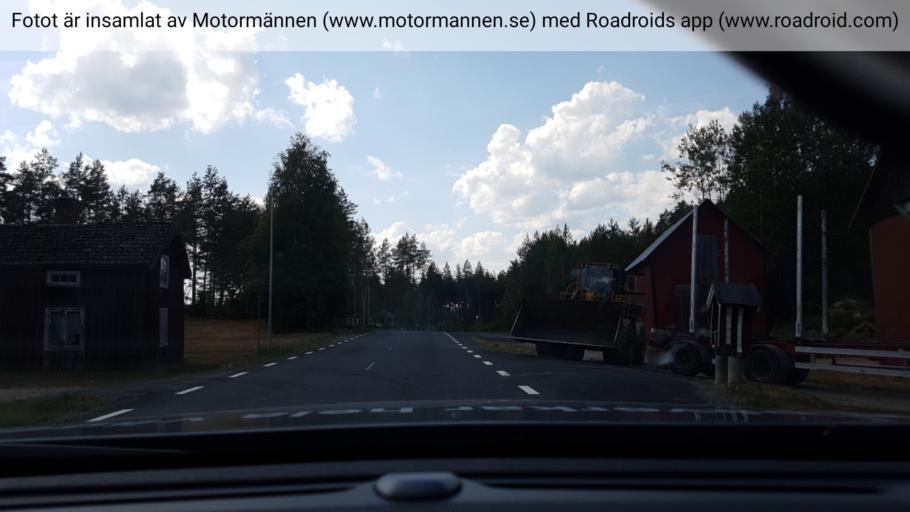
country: SE
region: Gaevleborg
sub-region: Hofors Kommun
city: Hofors
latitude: 60.7125
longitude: 16.2367
